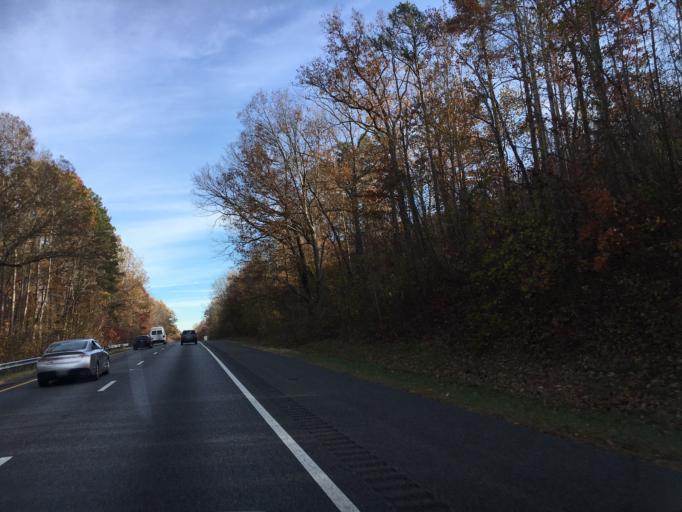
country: US
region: South Carolina
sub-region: Spartanburg County
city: Landrum
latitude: 35.1744
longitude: -82.1468
